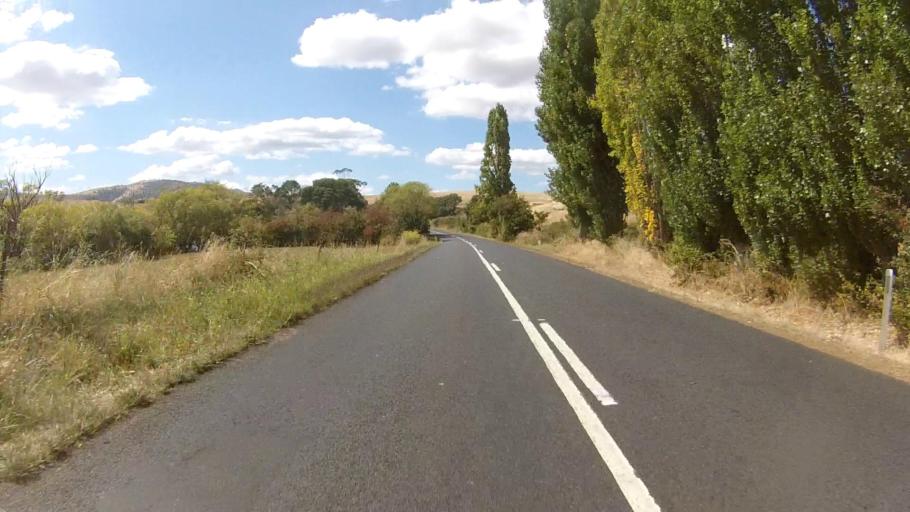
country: AU
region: Tasmania
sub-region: Derwent Valley
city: New Norfolk
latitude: -42.7334
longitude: 146.9197
